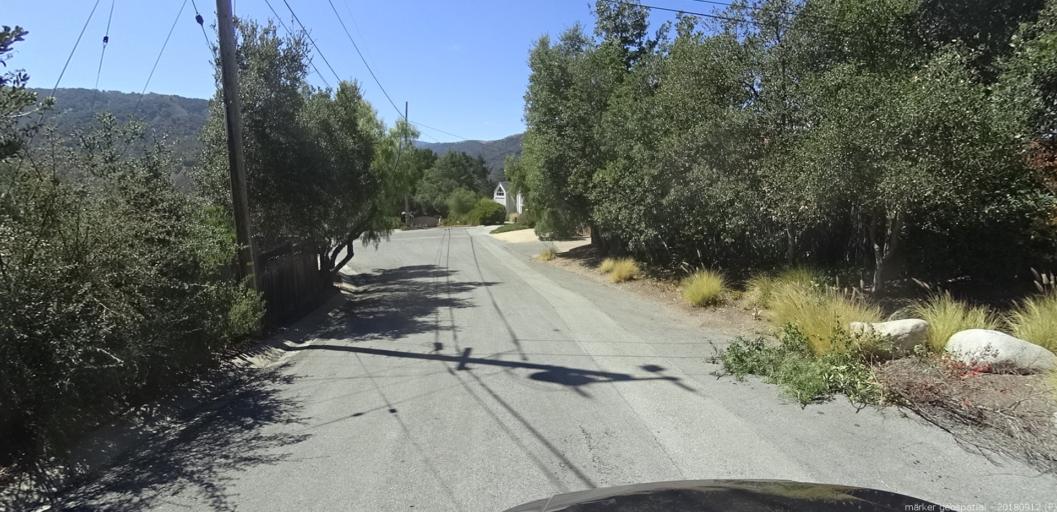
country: US
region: California
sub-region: Monterey County
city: Carmel Valley Village
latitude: 36.4933
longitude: -121.7387
